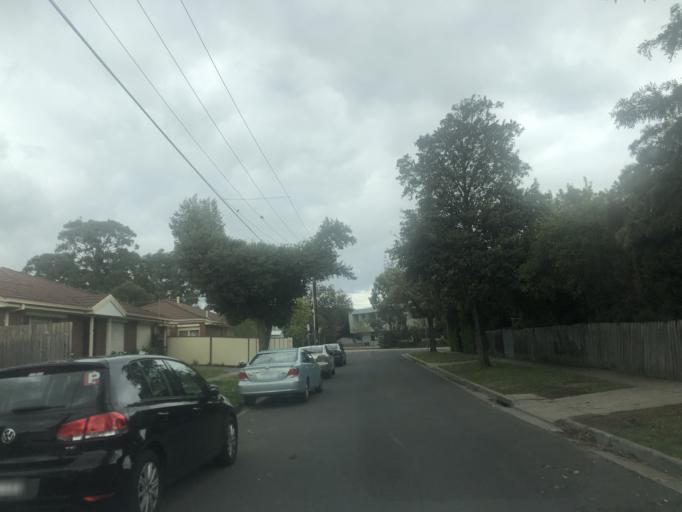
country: AU
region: Victoria
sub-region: Greater Dandenong
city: Dandenong
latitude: -37.9772
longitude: 145.2086
